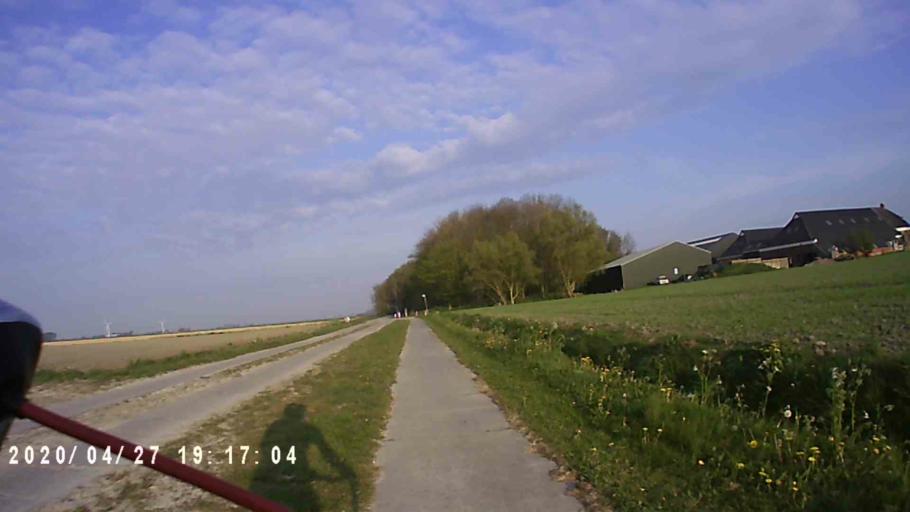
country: NL
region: Groningen
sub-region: Gemeente Winsum
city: Winsum
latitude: 53.4069
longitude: 6.4689
